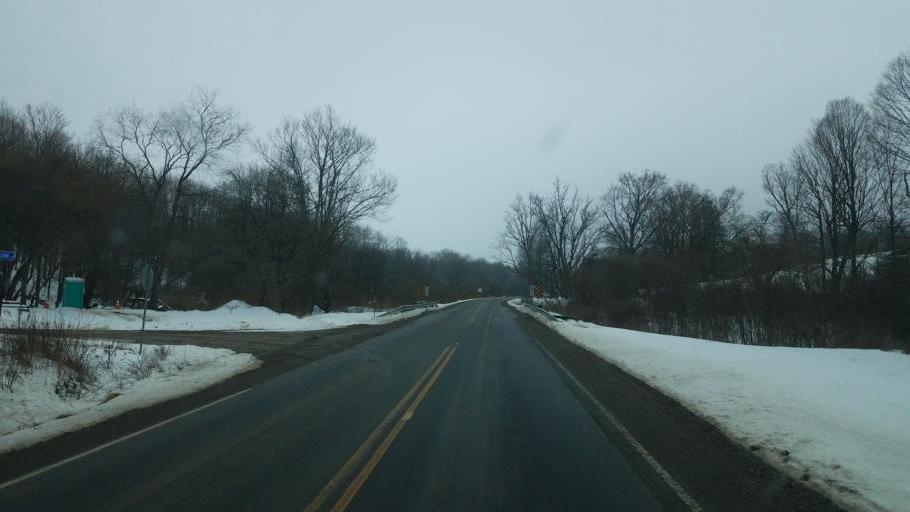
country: US
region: New York
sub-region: Allegany County
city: Andover
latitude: 42.0107
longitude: -77.7601
